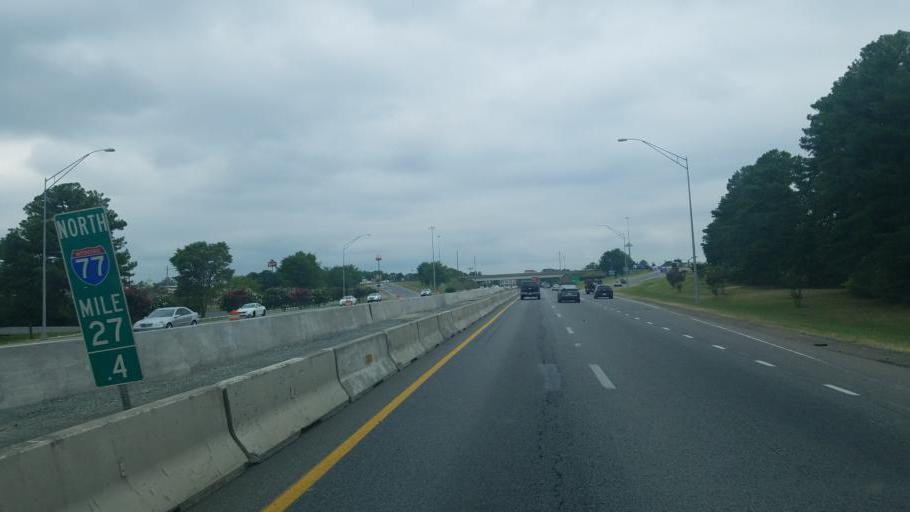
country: US
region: North Carolina
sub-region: Mecklenburg County
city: Cornelius
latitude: 35.4793
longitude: -80.8747
